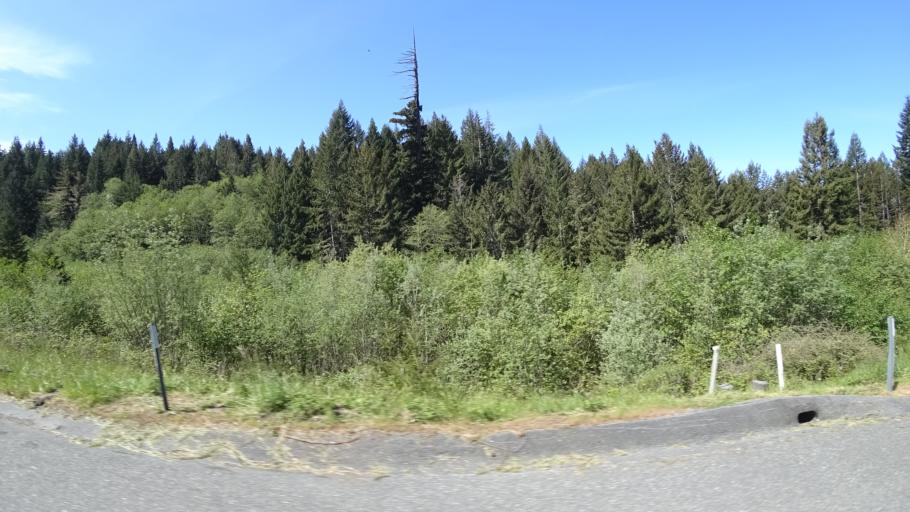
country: US
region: California
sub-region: Del Norte County
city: Bertsch-Oceanview
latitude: 41.4511
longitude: -124.0263
